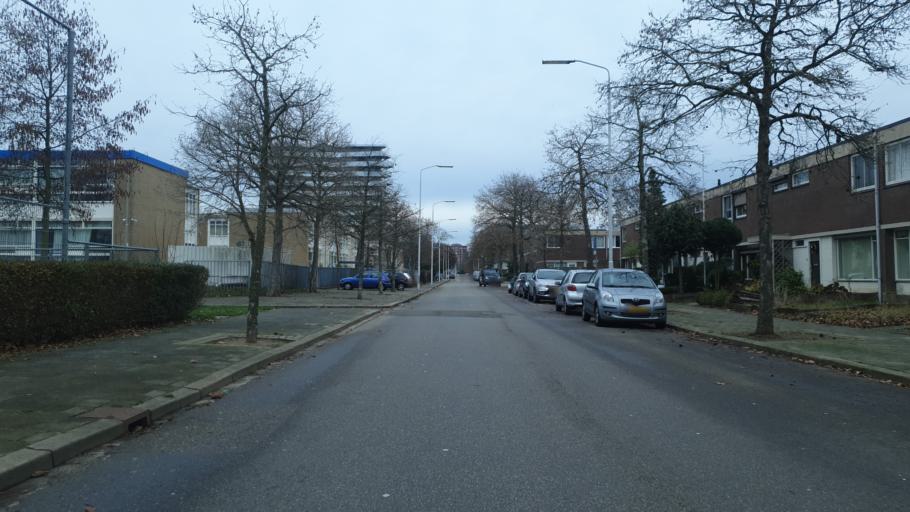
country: NL
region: Gelderland
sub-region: Gemeente Nijmegen
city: Lindenholt
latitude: 51.8033
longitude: 5.8257
